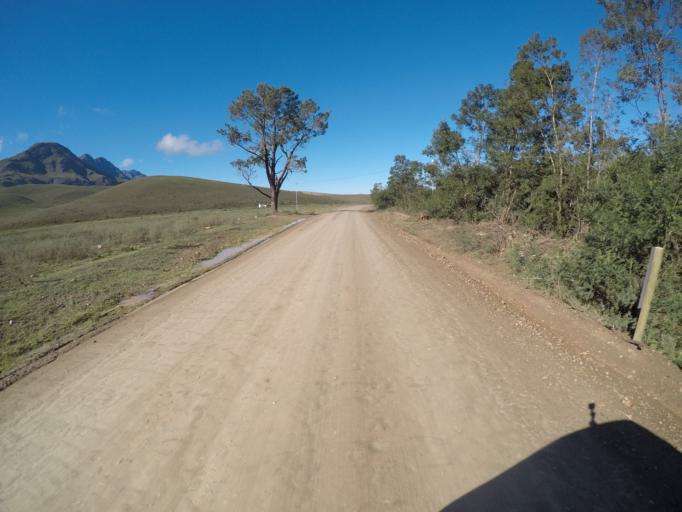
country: ZA
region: Western Cape
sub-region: Overberg District Municipality
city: Caledon
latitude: -34.0554
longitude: 19.6174
